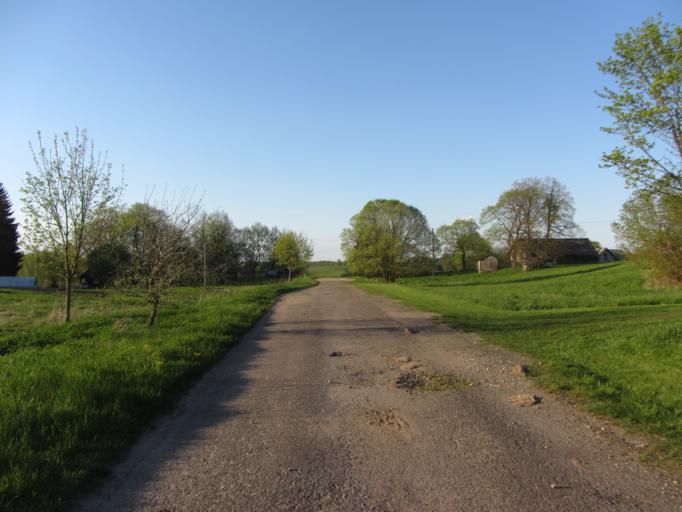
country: LT
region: Utenos apskritis
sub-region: Utena
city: Utena
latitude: 55.3750
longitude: 25.5209
